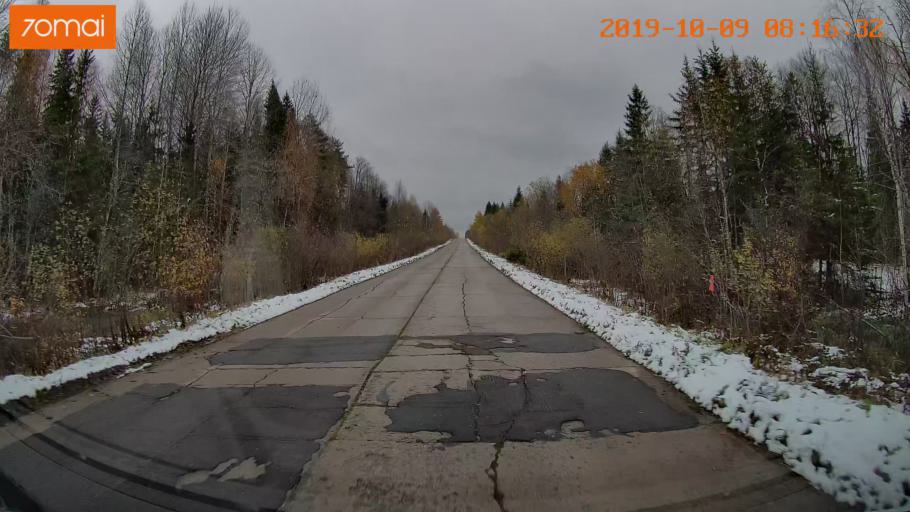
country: RU
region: Vologda
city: Gryazovets
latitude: 58.7372
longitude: 40.1896
